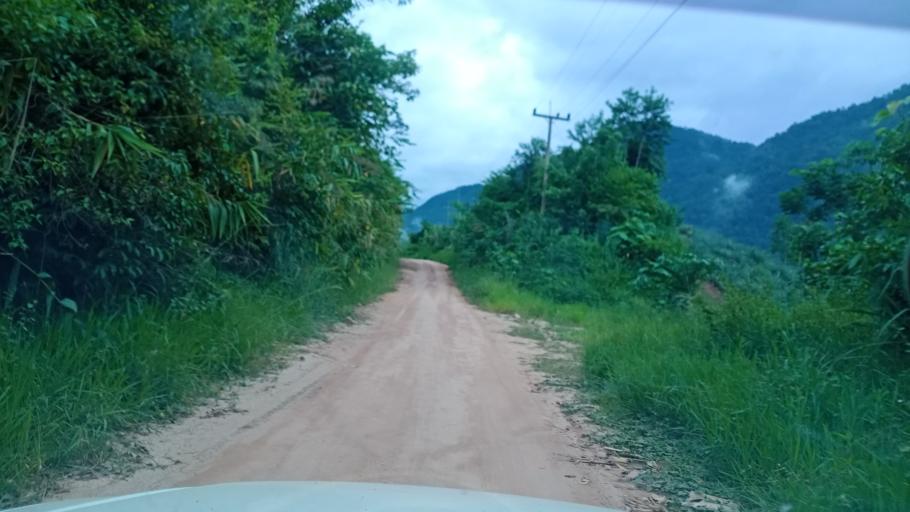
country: TH
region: Changwat Bueng Kan
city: Pak Khat
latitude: 18.7272
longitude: 103.2760
